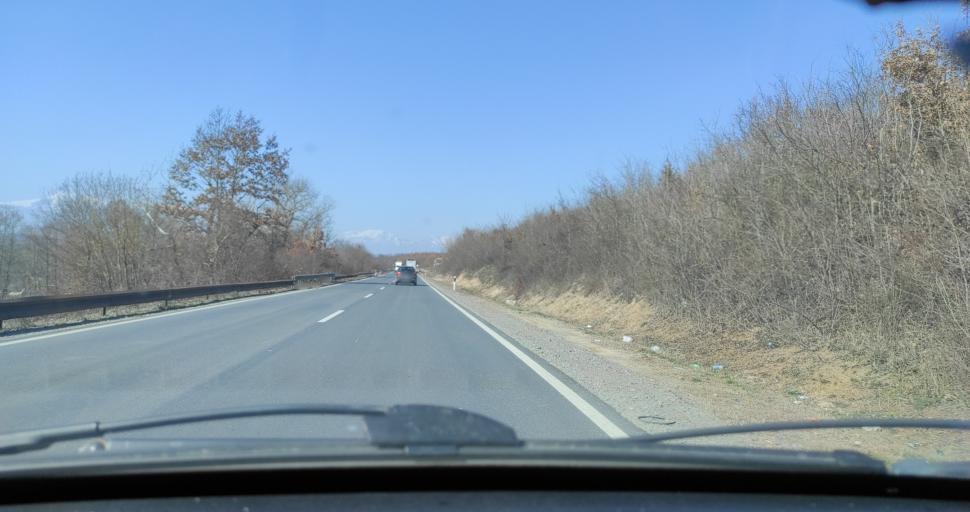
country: XK
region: Pec
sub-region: Komuna e Klines
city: Klina
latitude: 42.5941
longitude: 20.5432
